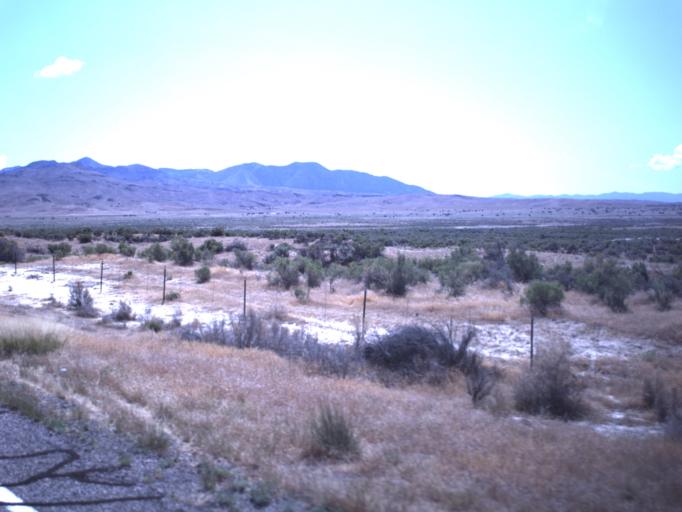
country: US
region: Utah
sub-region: Millard County
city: Delta
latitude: 39.3542
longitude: -112.4232
